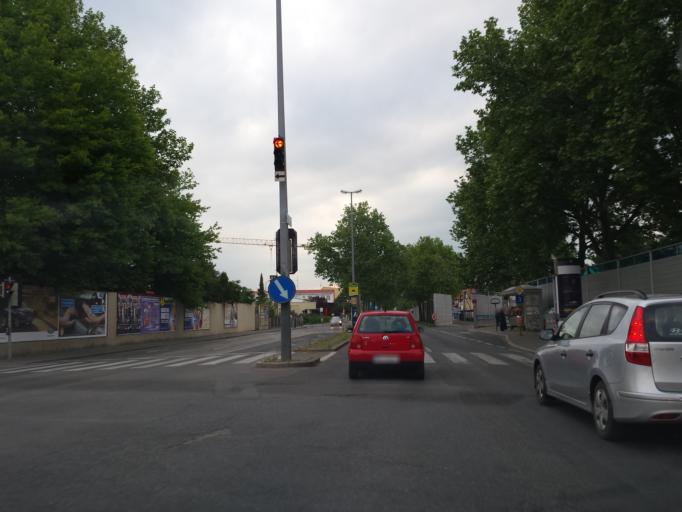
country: AT
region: Lower Austria
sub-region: Politischer Bezirk Wien-Umgebung
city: Gerasdorf bei Wien
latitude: 48.2256
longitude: 16.4648
